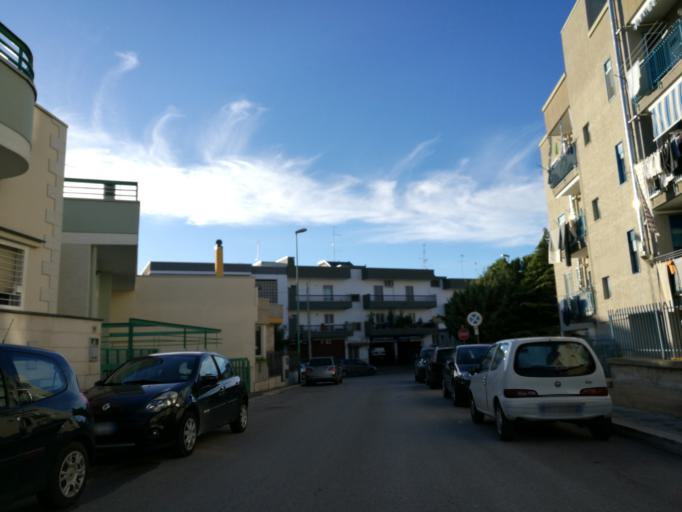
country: IT
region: Apulia
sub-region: Provincia di Bari
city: Adelfia
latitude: 41.0070
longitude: 16.8641
